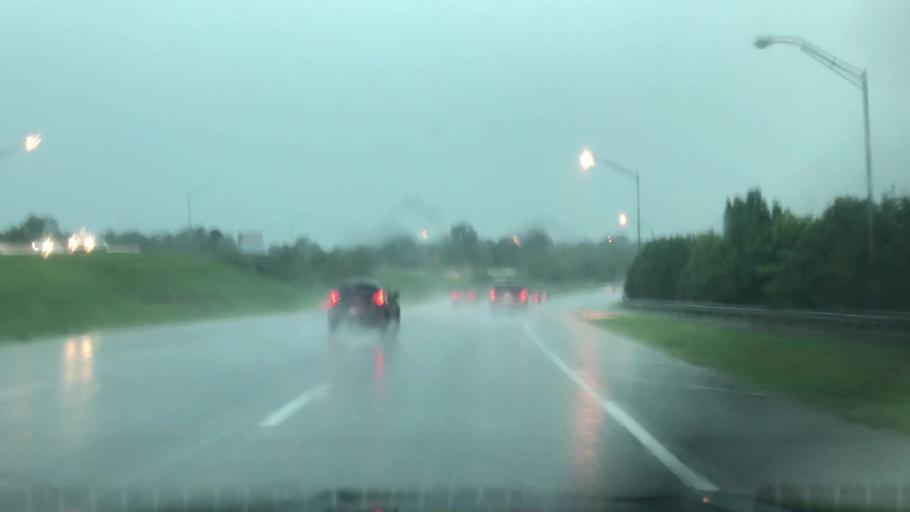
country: US
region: Oklahoma
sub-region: Tulsa County
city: Tulsa
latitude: 36.1152
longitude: -95.9073
